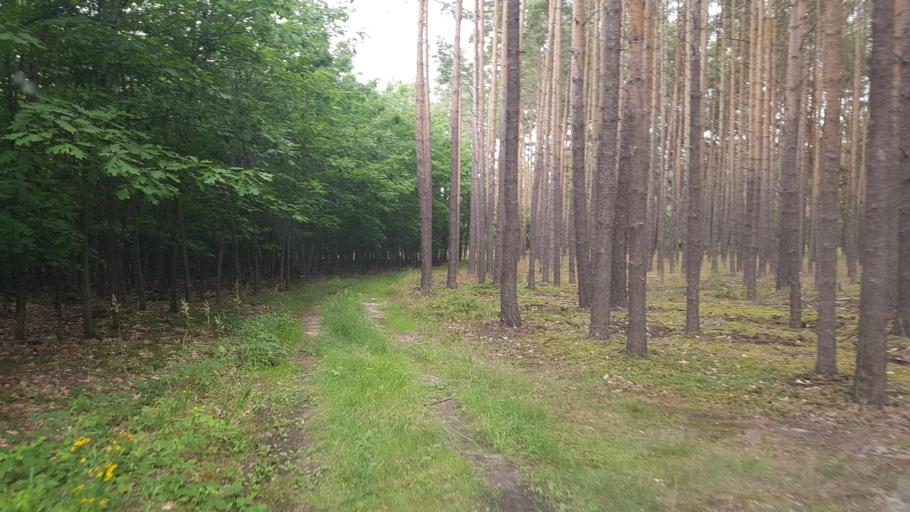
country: DE
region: Brandenburg
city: Crinitz
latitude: 51.7150
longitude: 13.7290
